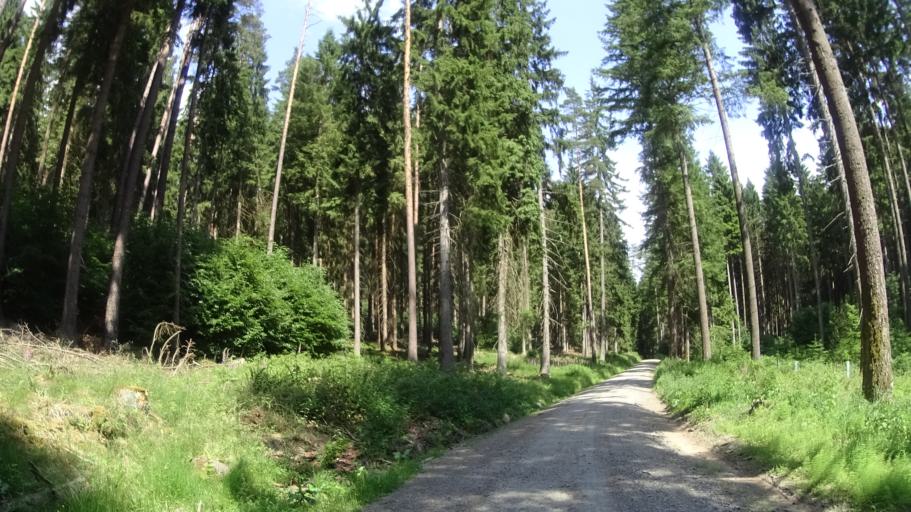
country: DE
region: Hesse
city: Rosenthal
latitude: 50.9658
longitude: 8.8252
